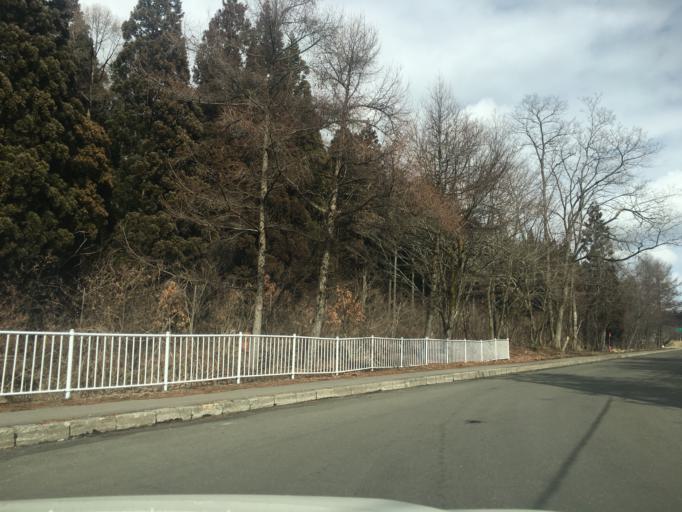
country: JP
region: Akita
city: Takanosu
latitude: 40.1860
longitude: 140.3394
